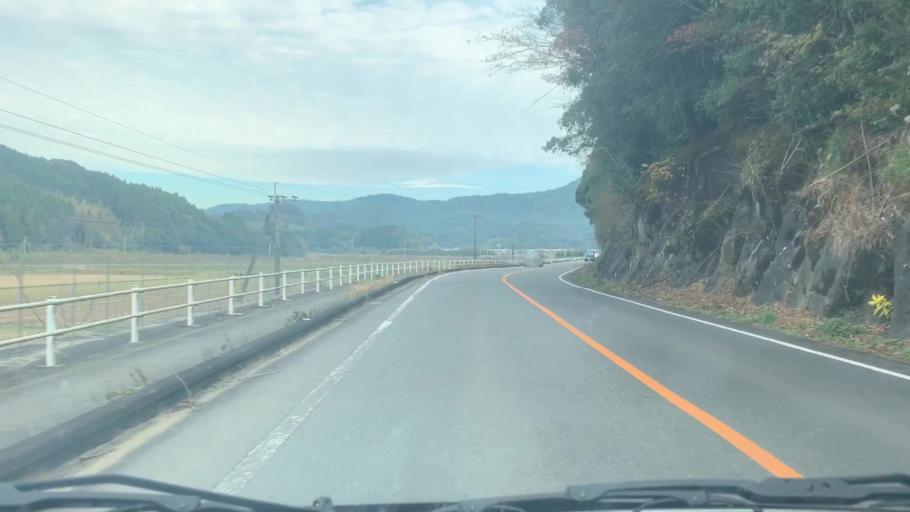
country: JP
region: Saga Prefecture
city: Takeocho-takeo
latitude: 33.2506
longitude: 129.9692
